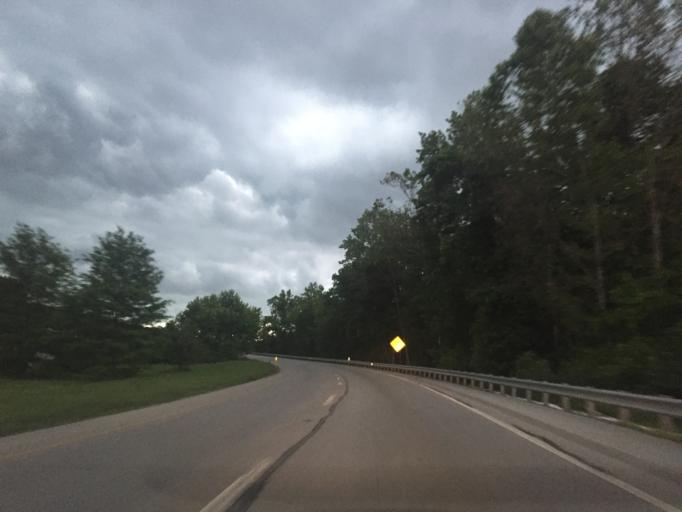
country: US
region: Pennsylvania
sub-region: York County
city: Grantley
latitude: 39.9437
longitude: -76.7193
